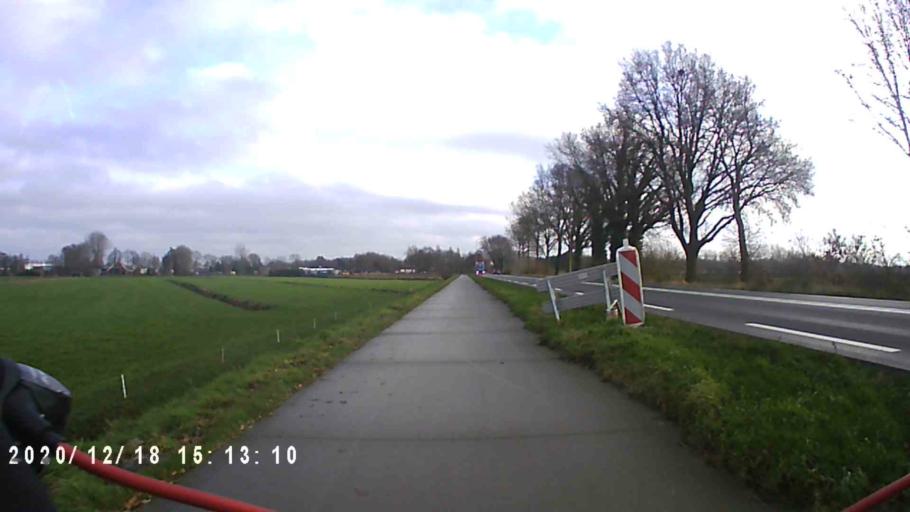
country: NL
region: Groningen
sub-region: Gemeente Hoogezand-Sappemeer
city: Hoogezand
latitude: 53.1638
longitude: 6.7162
